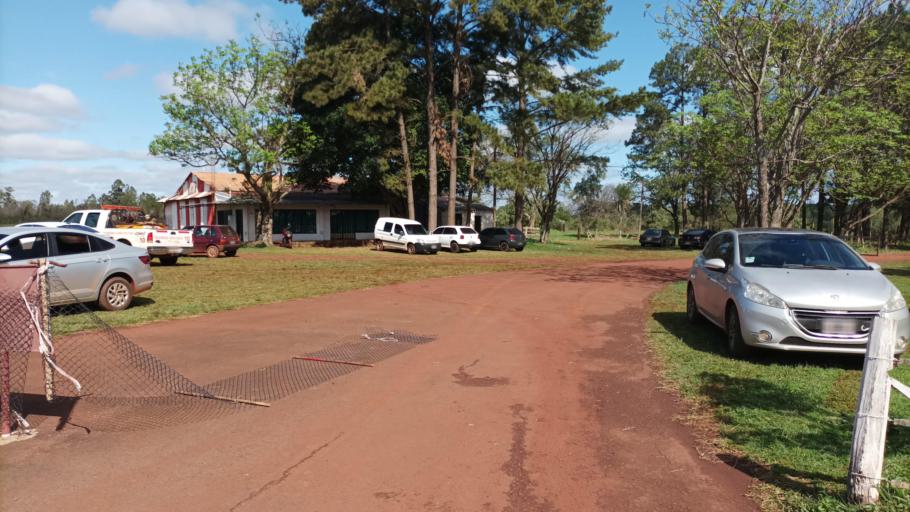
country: AR
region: Misiones
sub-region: Departamento de Apostoles
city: Apostoles
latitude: -27.9024
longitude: -55.7662
